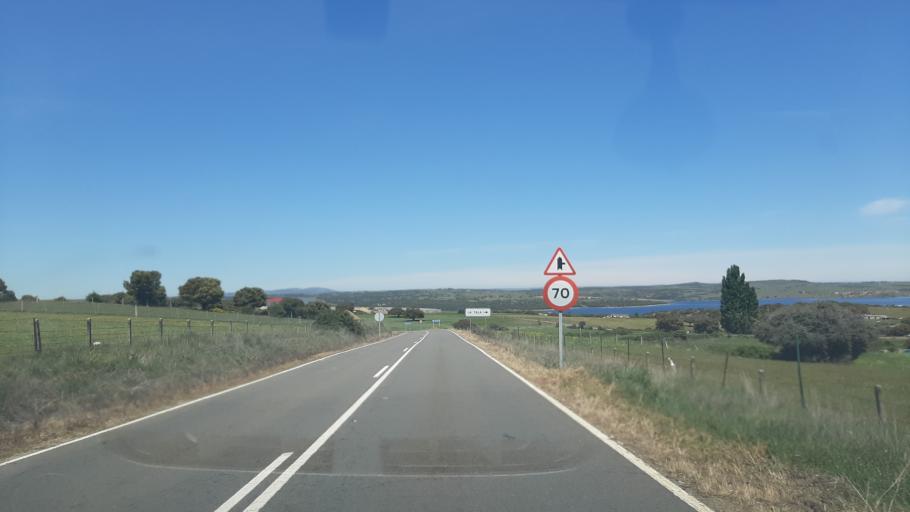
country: ES
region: Castille and Leon
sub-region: Provincia de Salamanca
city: Aldeavieja de Tormes
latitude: 40.5457
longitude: -5.5949
